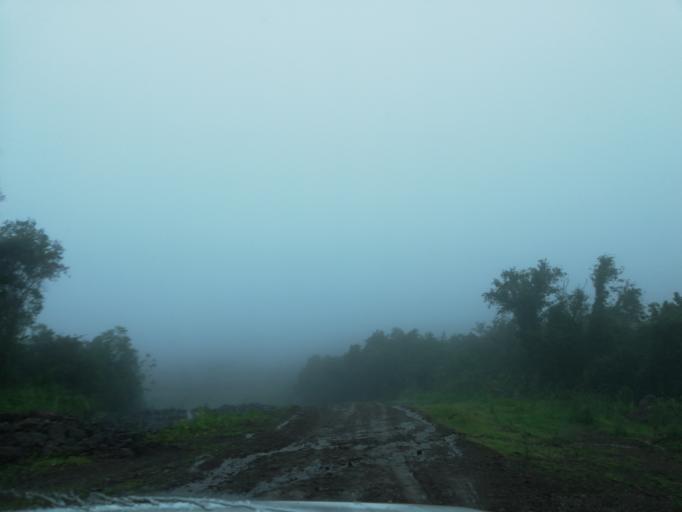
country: AR
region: Misiones
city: Almafuerte
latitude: -27.5351
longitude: -55.4096
